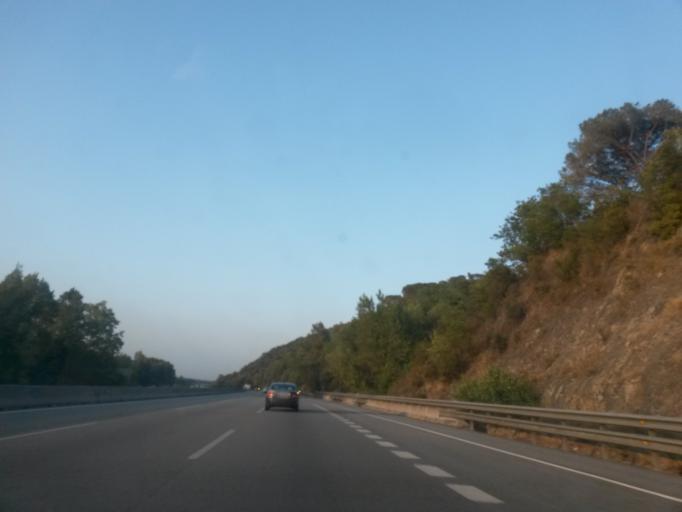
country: ES
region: Catalonia
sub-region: Provincia de Barcelona
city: Sant Celoni
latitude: 41.7056
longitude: 2.5264
